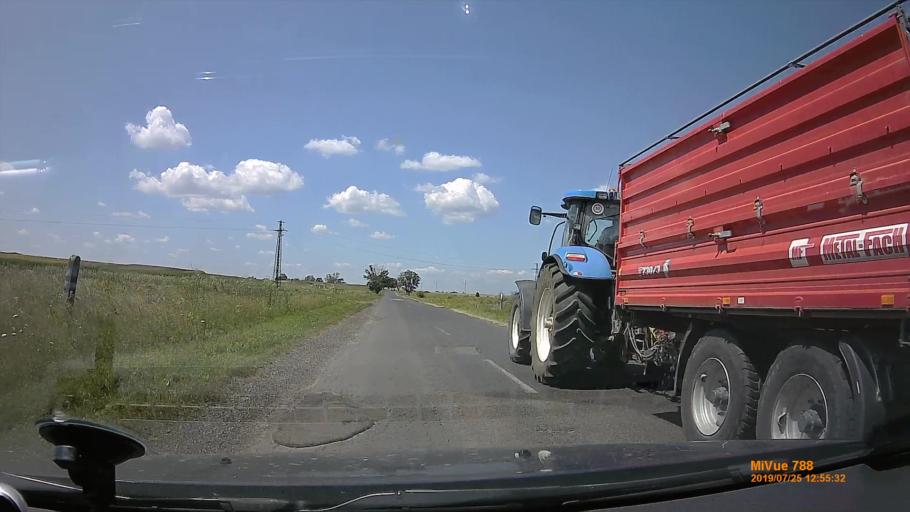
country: HU
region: Borsod-Abauj-Zemplen
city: Abaujszanto
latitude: 48.3103
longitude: 21.1863
